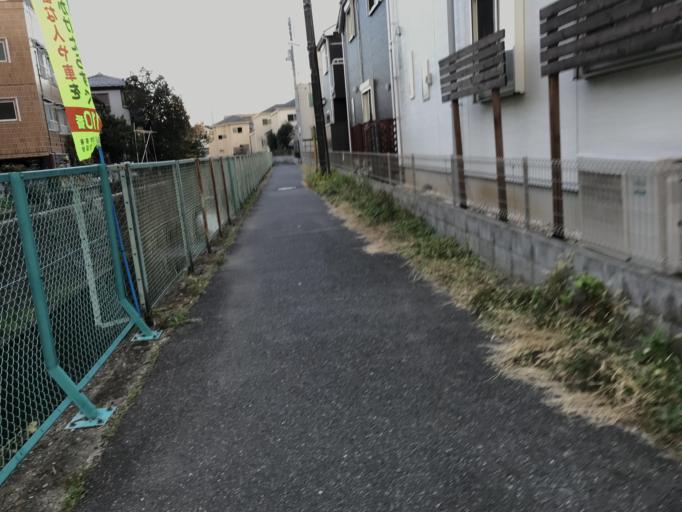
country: JP
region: Saitama
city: Wako
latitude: 35.7669
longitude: 139.6105
